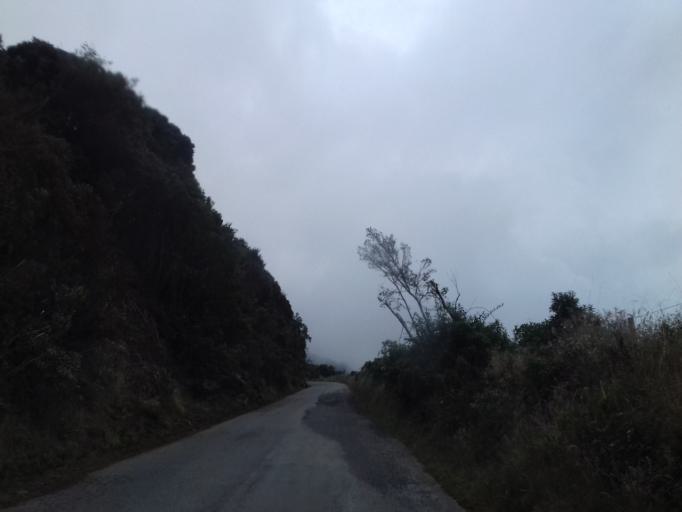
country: CO
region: Tolima
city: Herveo
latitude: 5.0115
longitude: -75.3296
